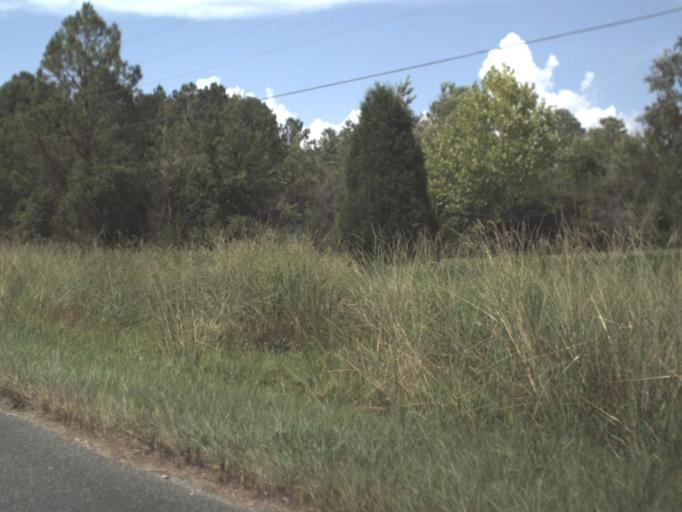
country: US
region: Florida
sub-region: Taylor County
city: Perry
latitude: 30.2562
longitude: -83.6240
